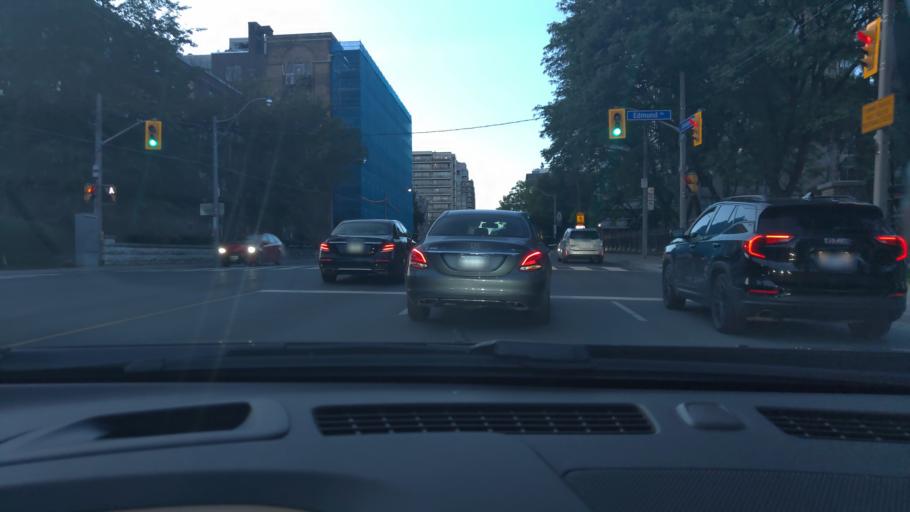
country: CA
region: Ontario
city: Toronto
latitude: 43.6822
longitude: -79.3996
